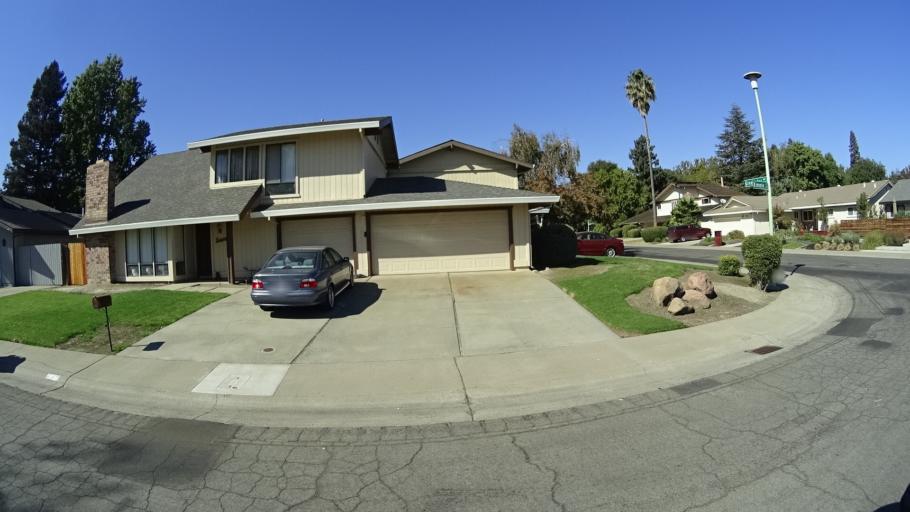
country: US
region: California
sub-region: Sacramento County
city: Parkway
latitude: 38.5002
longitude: -121.5262
